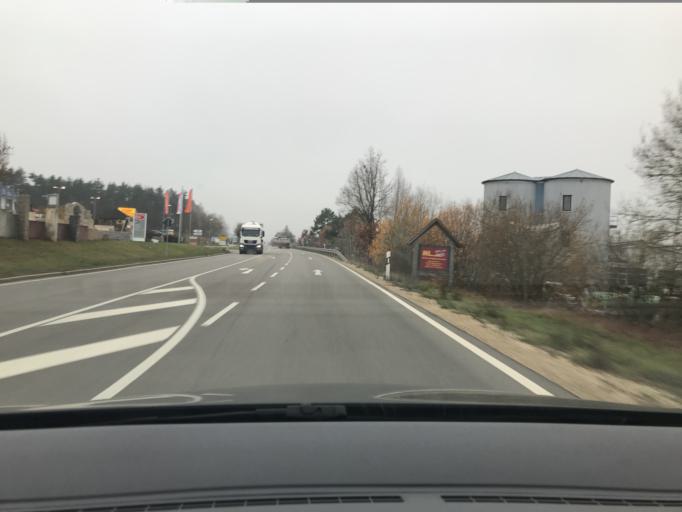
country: DE
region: Bavaria
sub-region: Regierungsbezirk Mittelfranken
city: Wilburgstetten
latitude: 49.0197
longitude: 10.3989
